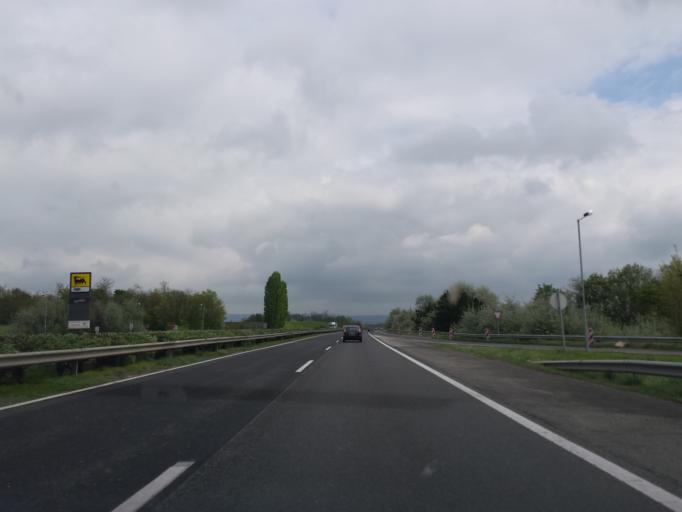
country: HU
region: Pest
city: Zsambek
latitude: 47.5108
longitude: 18.7368
